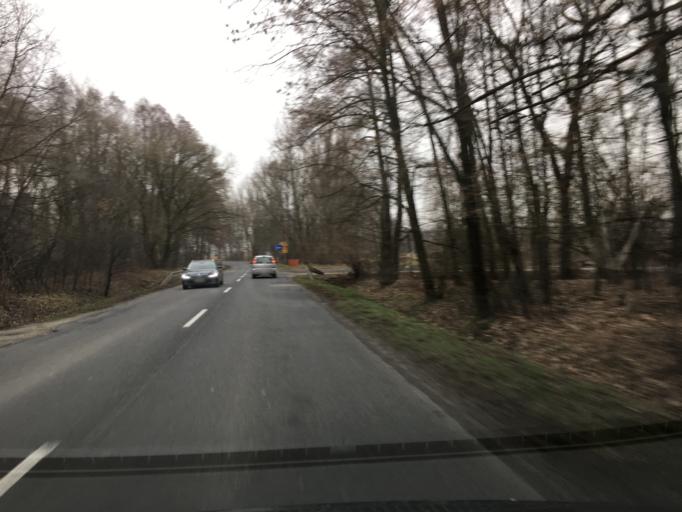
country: PL
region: Opole Voivodeship
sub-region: Powiat kedzierzynsko-kozielski
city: Bierawa
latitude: 50.2988
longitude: 18.2325
